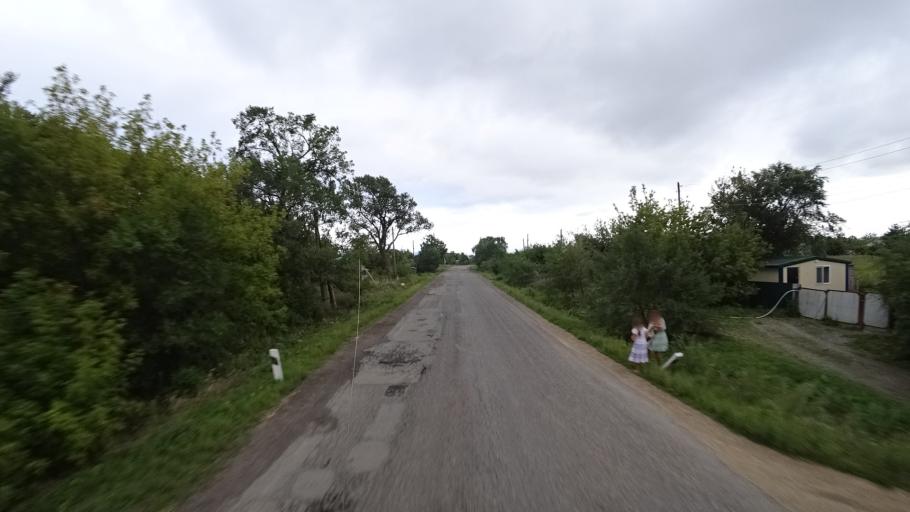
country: RU
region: Primorskiy
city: Chernigovka
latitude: 44.3526
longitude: 132.5678
